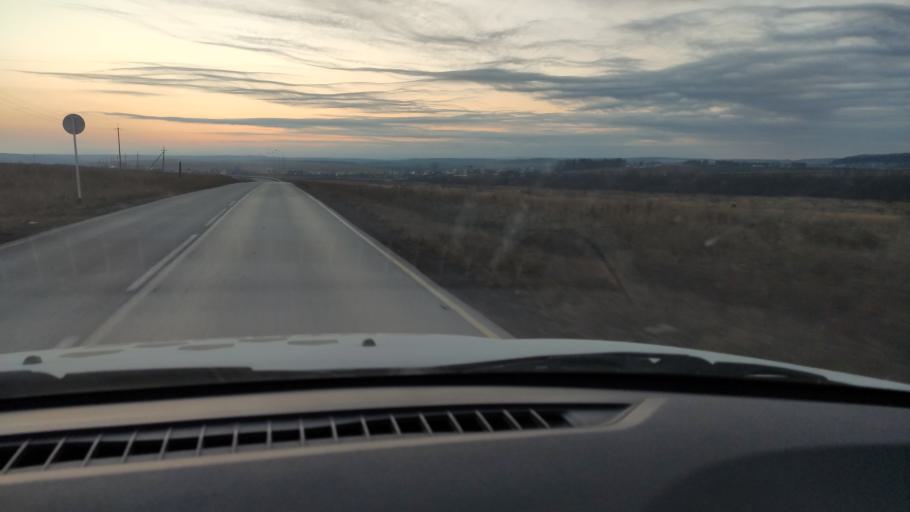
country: RU
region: Perm
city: Lobanovo
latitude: 57.8051
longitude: 56.3359
